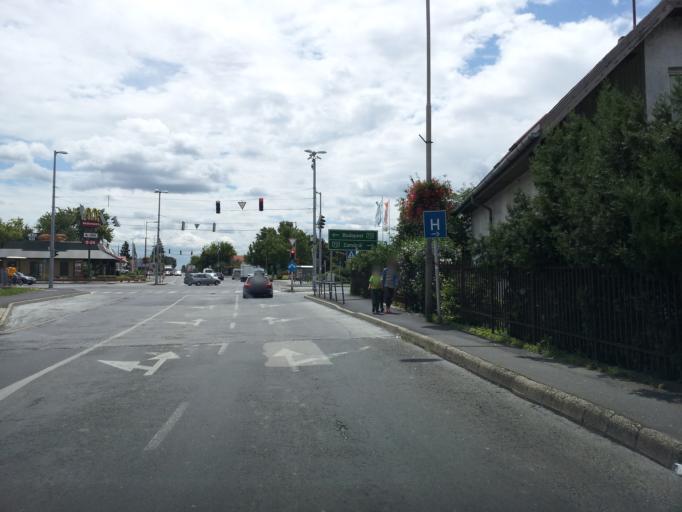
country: HU
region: Somogy
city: Siofok
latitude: 46.9029
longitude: 18.0473
